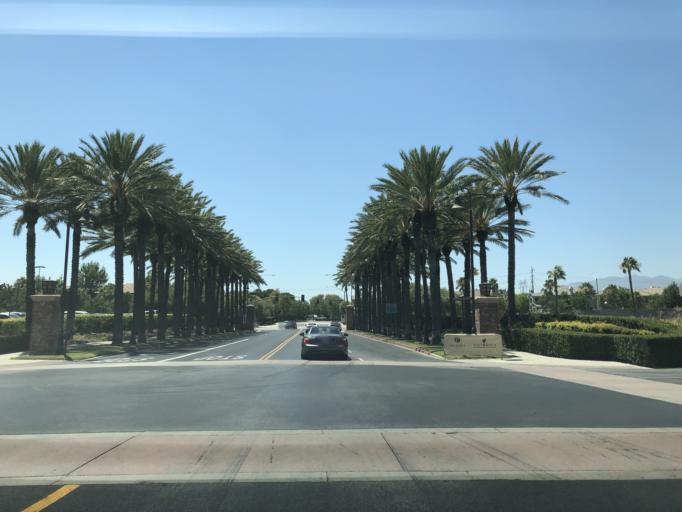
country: US
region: California
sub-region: San Bernardino County
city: Rancho Cucamonga
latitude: 34.1121
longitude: -117.5355
